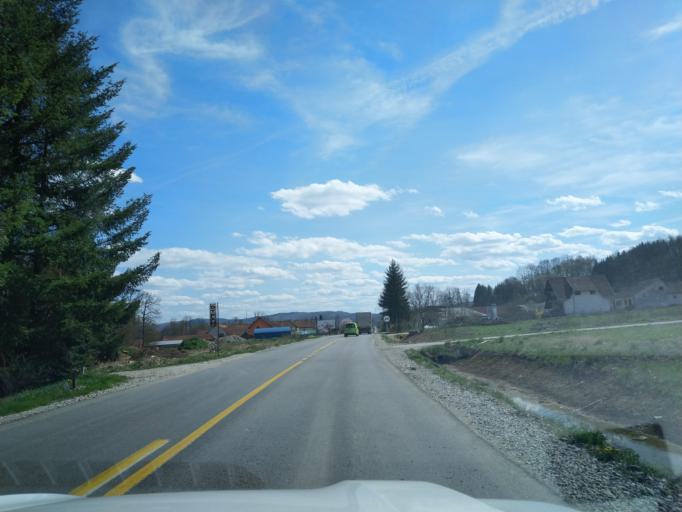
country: RS
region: Central Serbia
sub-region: Zlatiborski Okrug
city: Pozega
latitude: 43.8193
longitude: 20.0856
